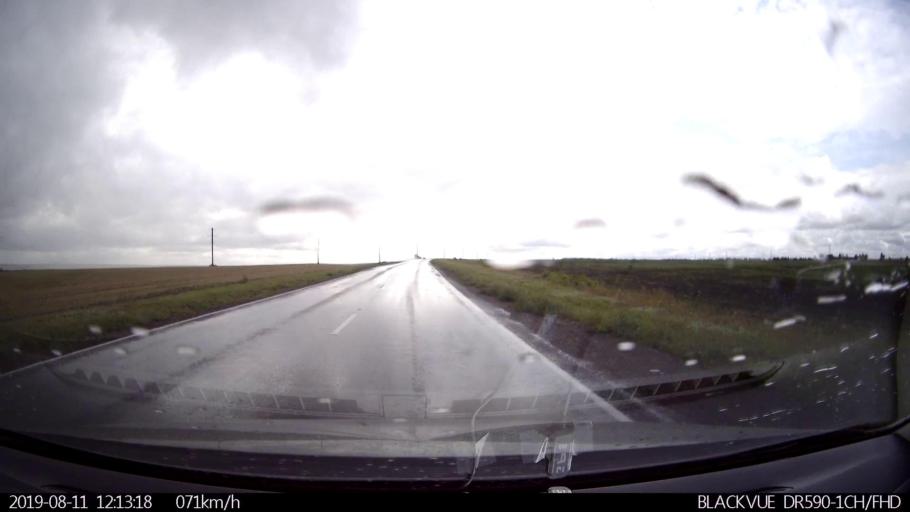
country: RU
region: Ulyanovsk
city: Silikatnyy
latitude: 53.9634
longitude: 47.9930
